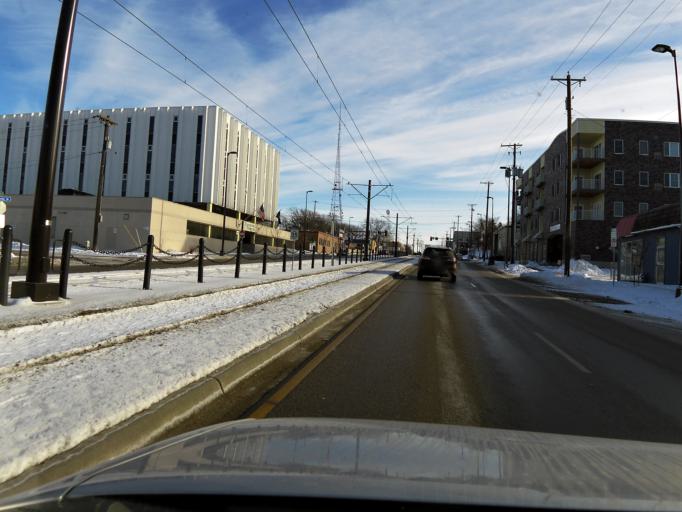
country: US
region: Minnesota
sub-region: Ramsey County
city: Lauderdale
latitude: 44.9705
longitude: -93.2144
